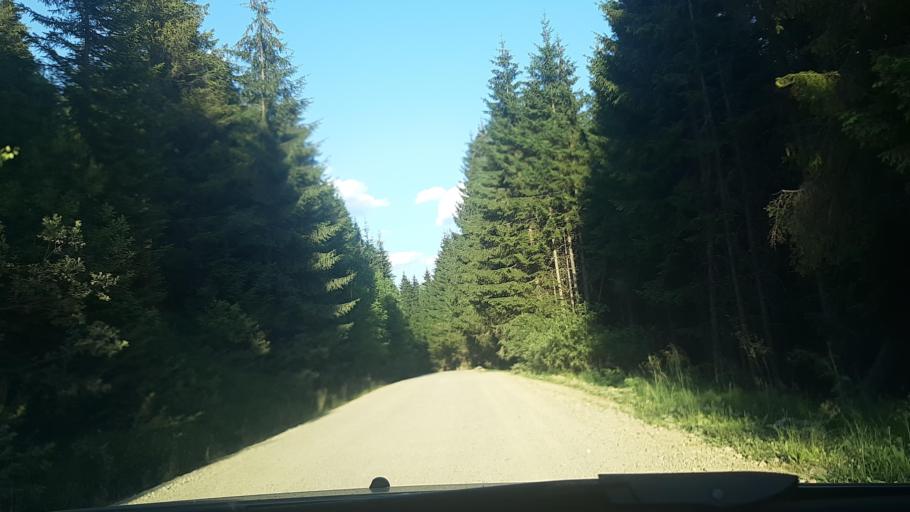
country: RO
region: Alba
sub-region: Comuna Sugag
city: Sugag
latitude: 45.5852
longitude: 23.6155
